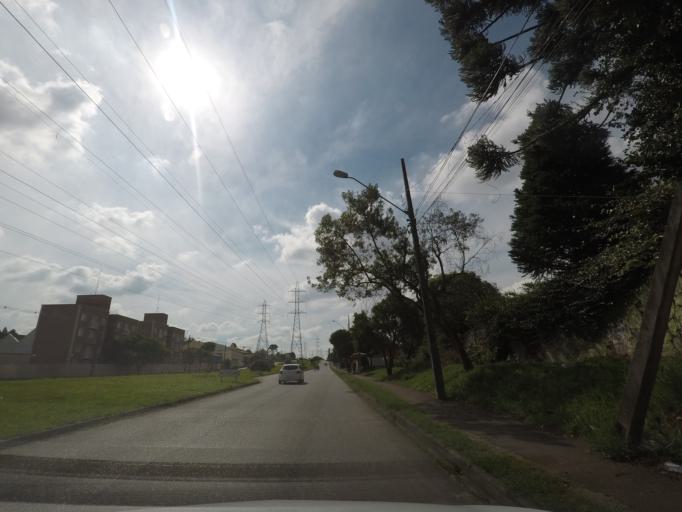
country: BR
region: Parana
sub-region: Pinhais
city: Pinhais
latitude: -25.4857
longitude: -49.2073
